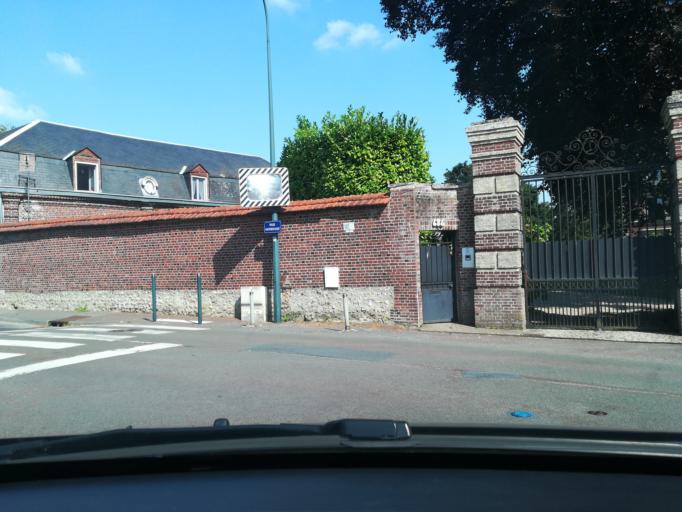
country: FR
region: Haute-Normandie
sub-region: Departement de la Seine-Maritime
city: Bois-Guillaume
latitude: 49.4658
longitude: 1.1260
